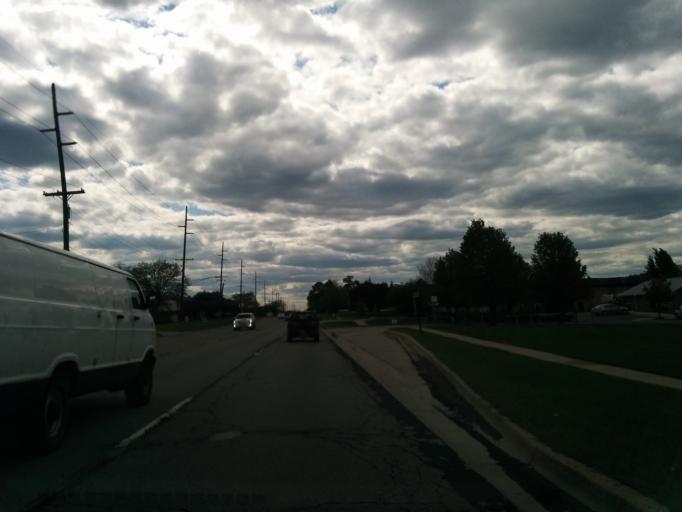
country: US
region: Michigan
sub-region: Oakland County
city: Farmington Hills
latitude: 42.4991
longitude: -83.3642
